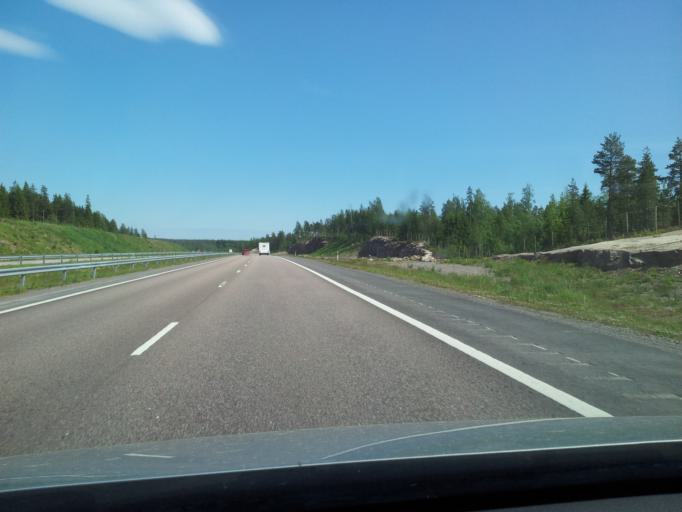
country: FI
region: Uusimaa
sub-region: Loviisa
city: Perna
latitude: 60.4813
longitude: 26.0282
